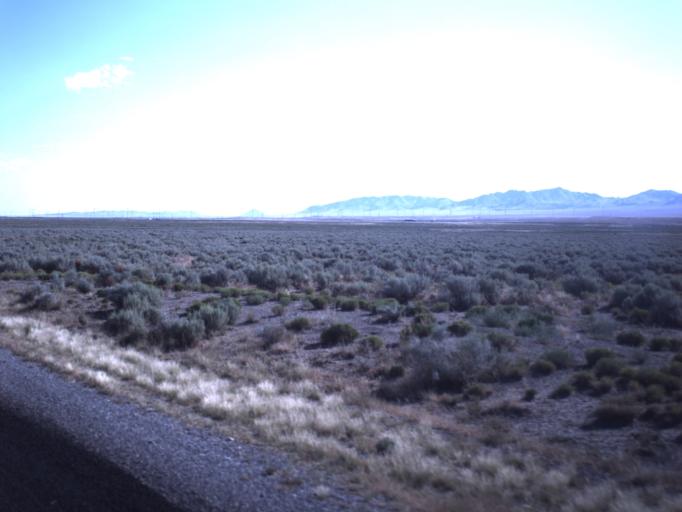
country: US
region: Utah
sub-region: Beaver County
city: Milford
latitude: 38.4410
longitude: -113.0097
